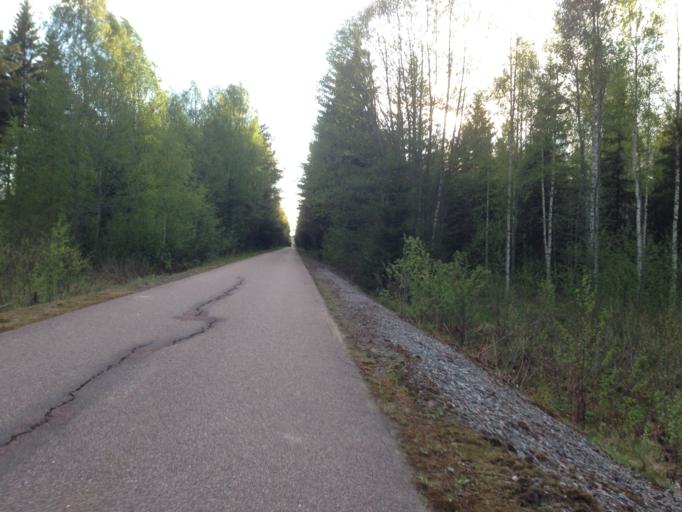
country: SE
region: Dalarna
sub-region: Ludvika Kommun
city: Ludvika
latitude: 60.1391
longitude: 15.1276
